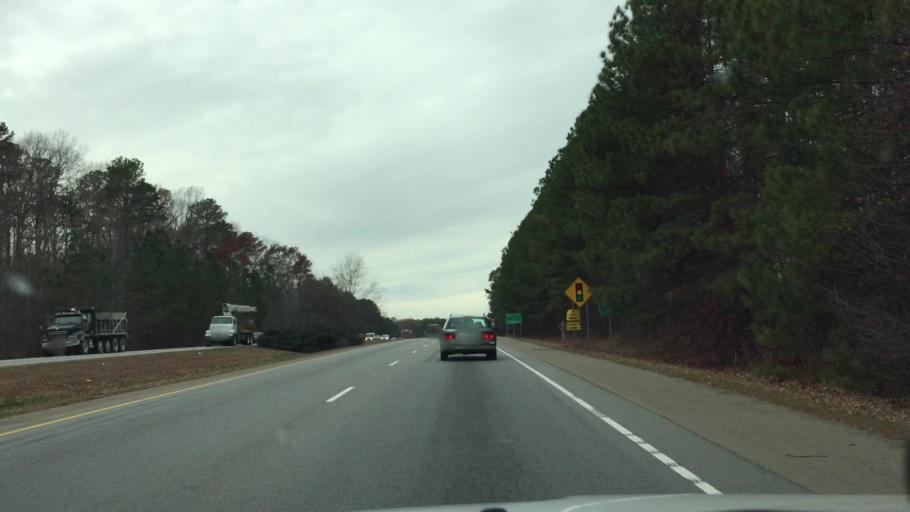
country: US
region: North Carolina
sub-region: Wake County
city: Apex
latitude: 35.7430
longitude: -78.8169
